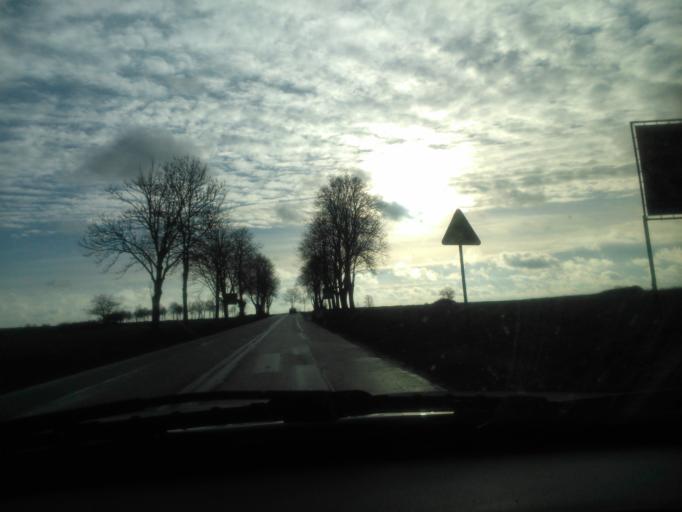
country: PL
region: Podlasie
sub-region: Powiat kolnenski
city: Kolno
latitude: 53.4233
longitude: 21.8899
